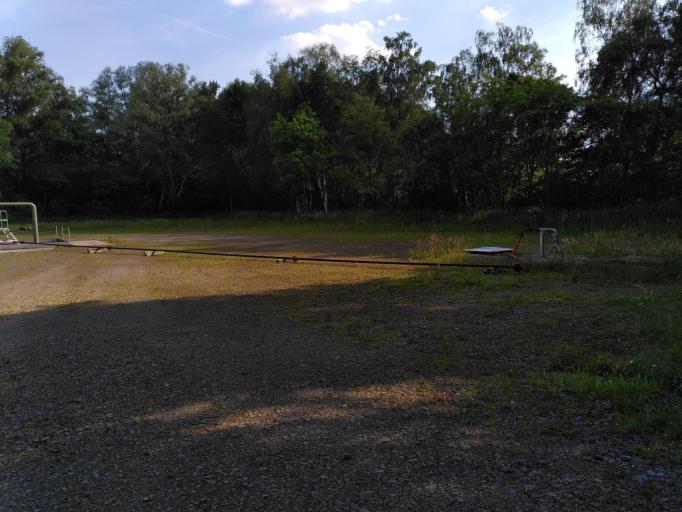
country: DE
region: North Rhine-Westphalia
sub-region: Regierungsbezirk Munster
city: Gronau
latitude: 52.1623
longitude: 6.9865
